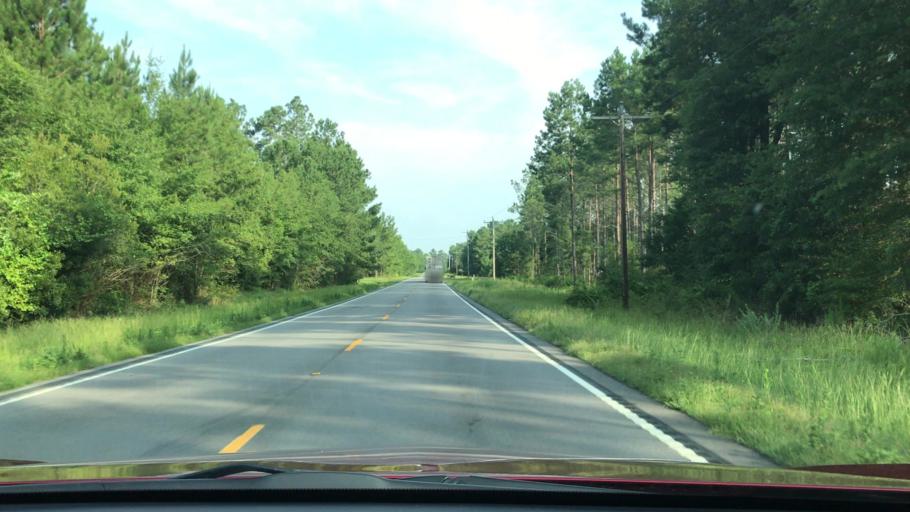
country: US
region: South Carolina
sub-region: Barnwell County
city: Blackville
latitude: 33.5486
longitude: -81.1549
